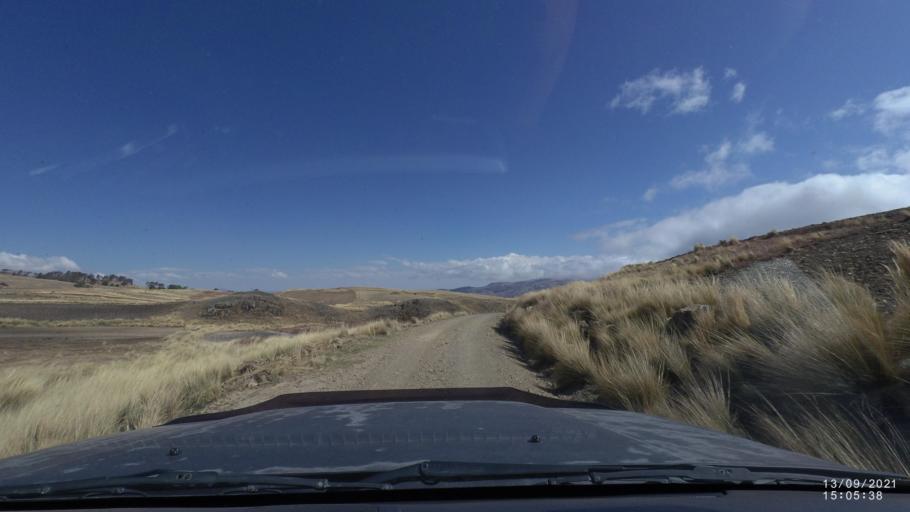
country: BO
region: Cochabamba
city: Colomi
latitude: -17.3449
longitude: -65.7920
